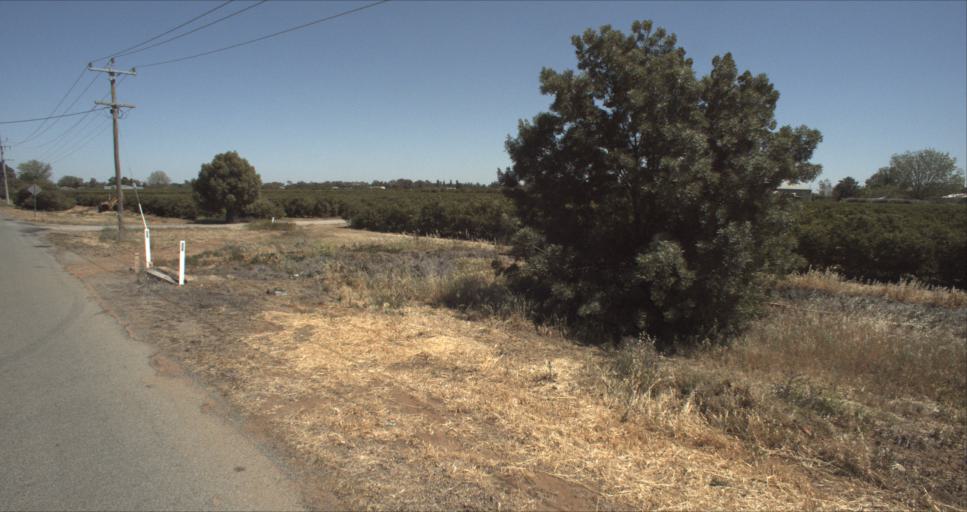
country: AU
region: New South Wales
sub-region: Leeton
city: Leeton
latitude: -34.5347
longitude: 146.3984
